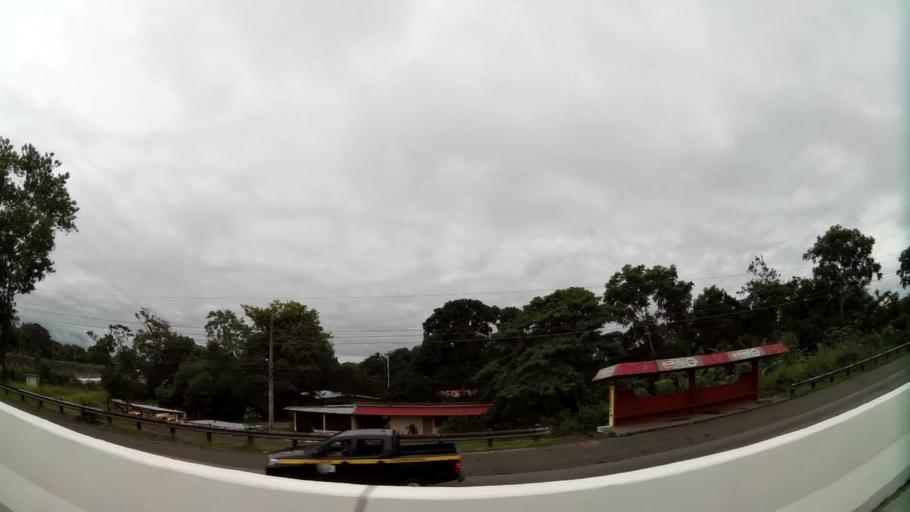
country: PA
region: Chiriqui
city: Bugaba
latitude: 8.4987
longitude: -82.5960
